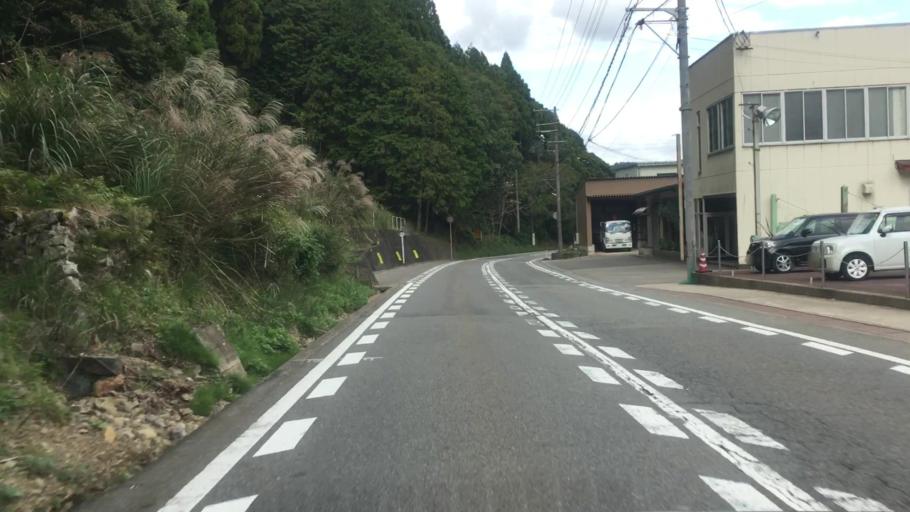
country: JP
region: Hyogo
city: Toyooka
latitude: 35.3651
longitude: 134.7602
